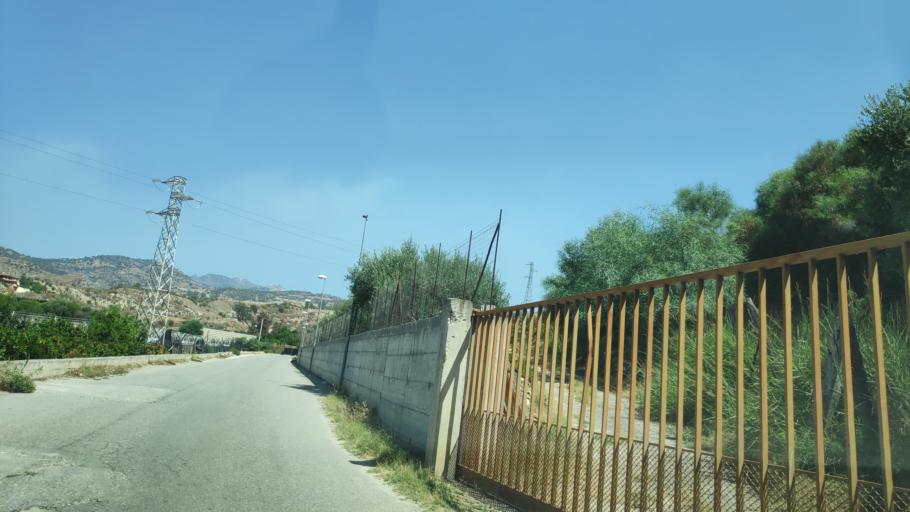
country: IT
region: Calabria
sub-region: Provincia di Reggio Calabria
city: Bova Marina
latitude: 37.9330
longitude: 15.9112
